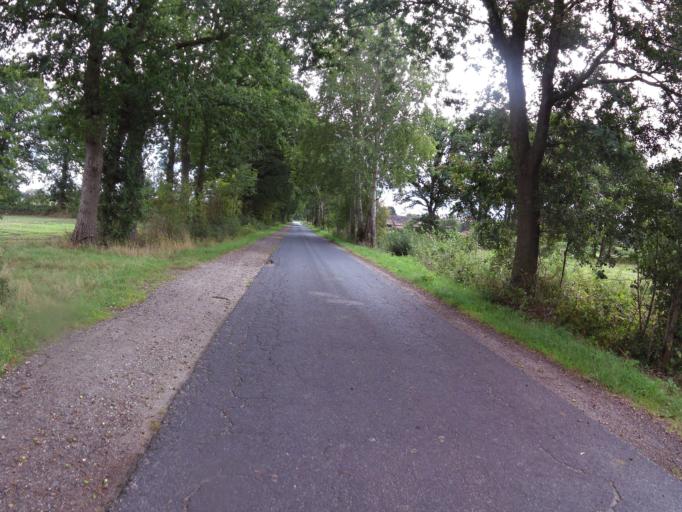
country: DE
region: Lower Saxony
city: Schiffdorf
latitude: 53.5017
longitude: 8.7009
